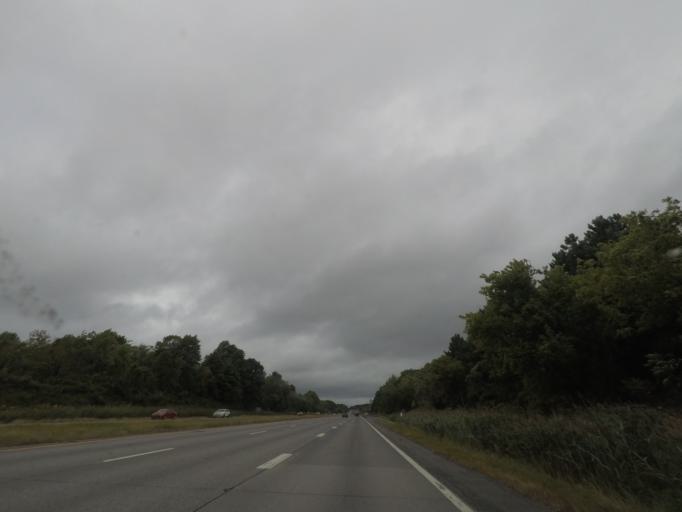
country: US
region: New York
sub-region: Albany County
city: Watervliet
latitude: 42.7518
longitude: -73.7194
